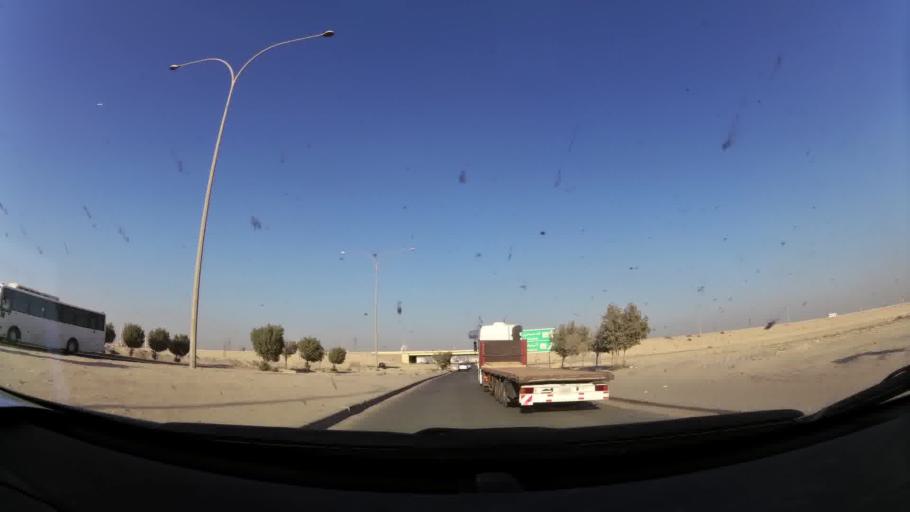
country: KW
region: Al Ahmadi
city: Al Fahahil
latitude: 29.0090
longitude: 48.1308
